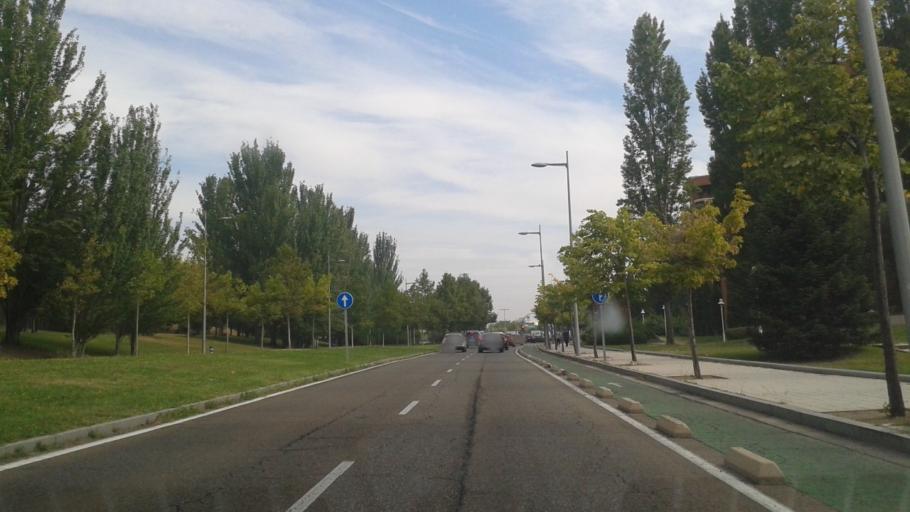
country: ES
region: Castille and Leon
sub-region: Provincia de Valladolid
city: Valladolid
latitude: 41.6322
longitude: -4.7516
